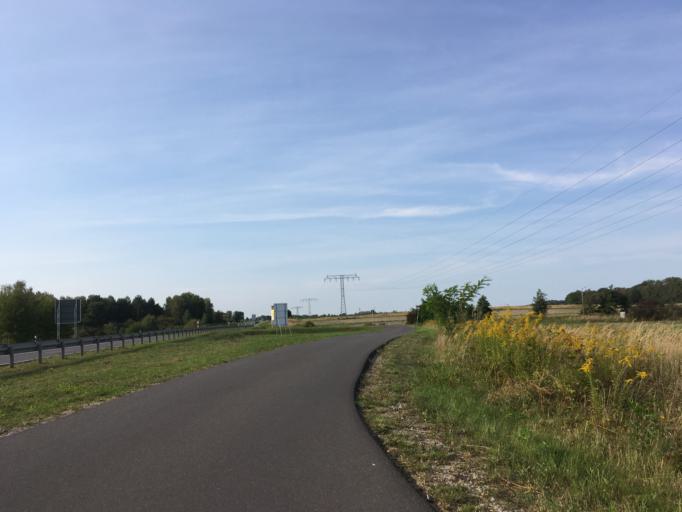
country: DE
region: Brandenburg
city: Brieskow-Finkenheerd
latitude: 52.2692
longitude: 14.5696
